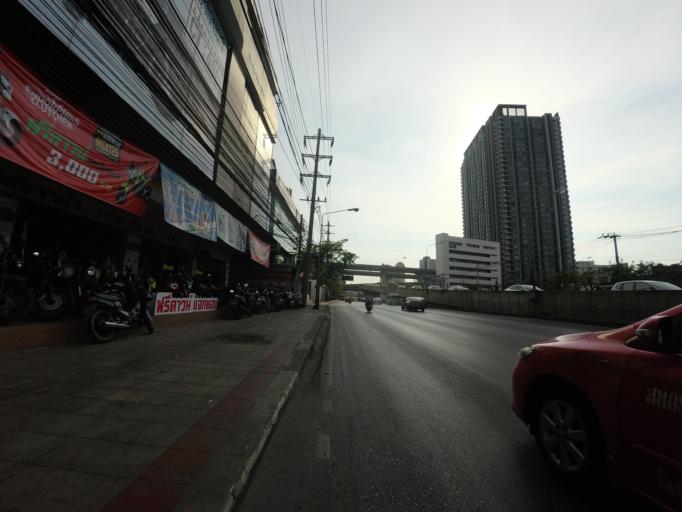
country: TH
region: Bangkok
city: Watthana
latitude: 13.7490
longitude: 100.6072
